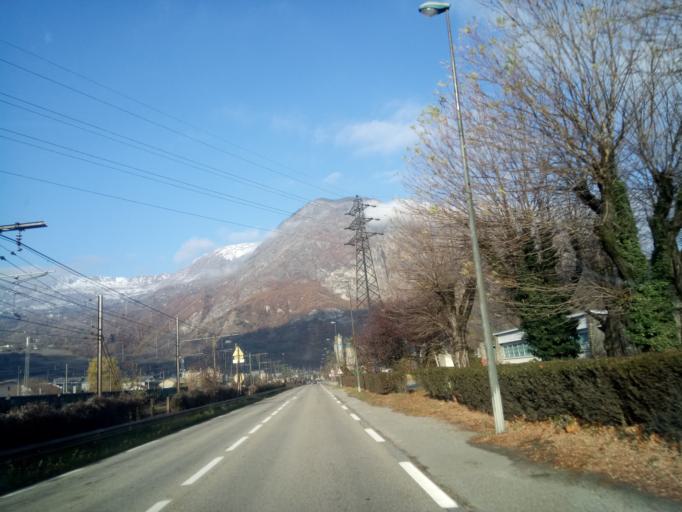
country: FR
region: Rhone-Alpes
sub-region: Departement de la Savoie
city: Villargondran
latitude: 45.2740
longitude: 6.3629
